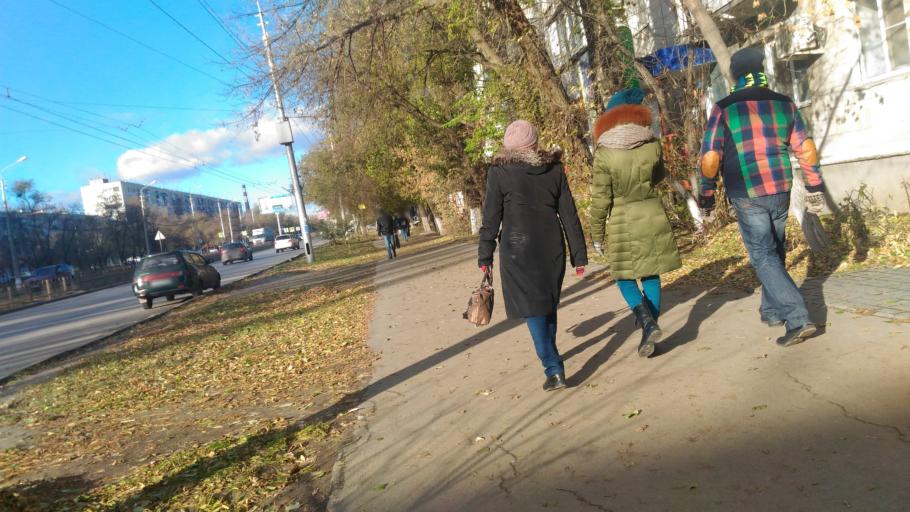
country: RU
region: Volgograd
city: Volgograd
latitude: 48.6029
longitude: 44.4221
